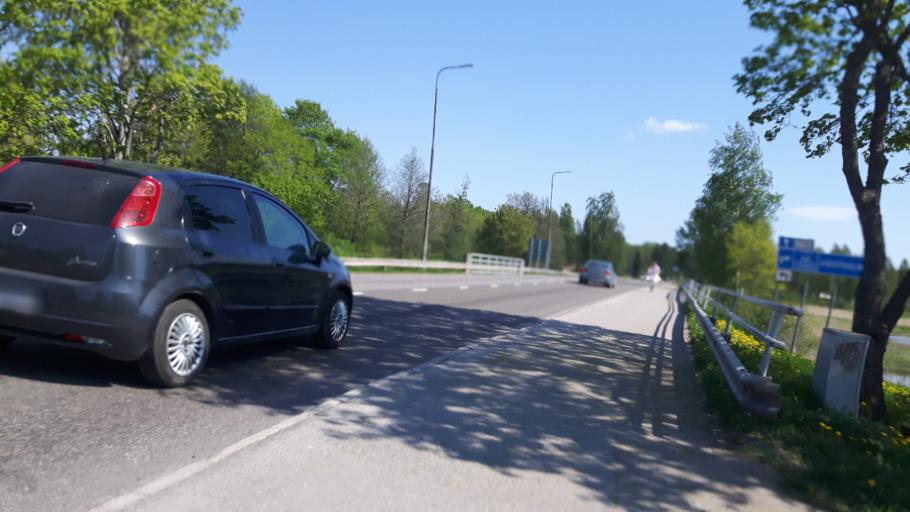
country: FI
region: Uusimaa
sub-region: Loviisa
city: Lovisa
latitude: 60.4593
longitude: 26.2335
